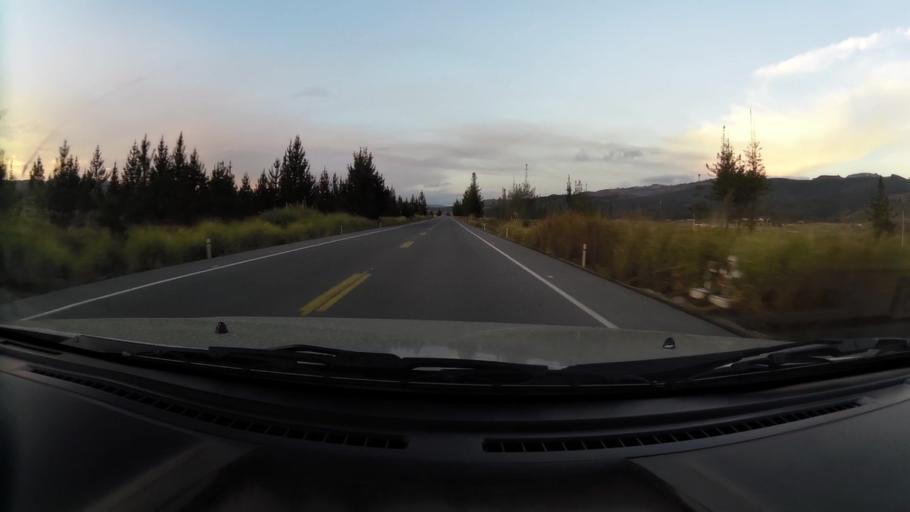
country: EC
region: Chimborazo
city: Alausi
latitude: -2.0217
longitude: -78.7320
